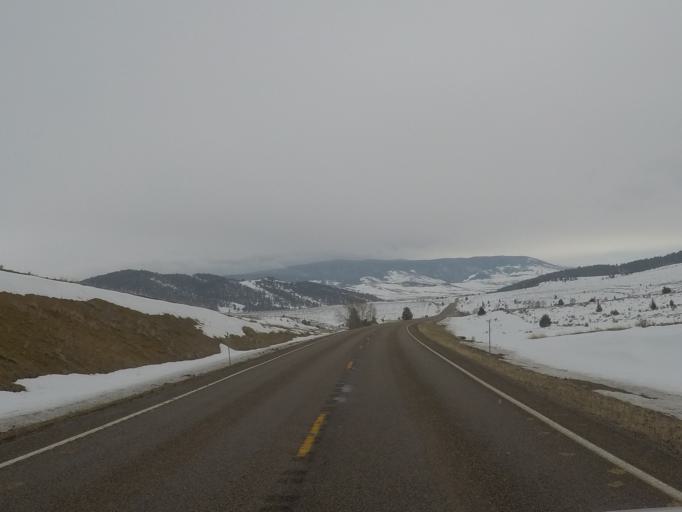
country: US
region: Montana
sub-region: Meagher County
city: White Sulphur Springs
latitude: 46.6293
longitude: -110.8494
